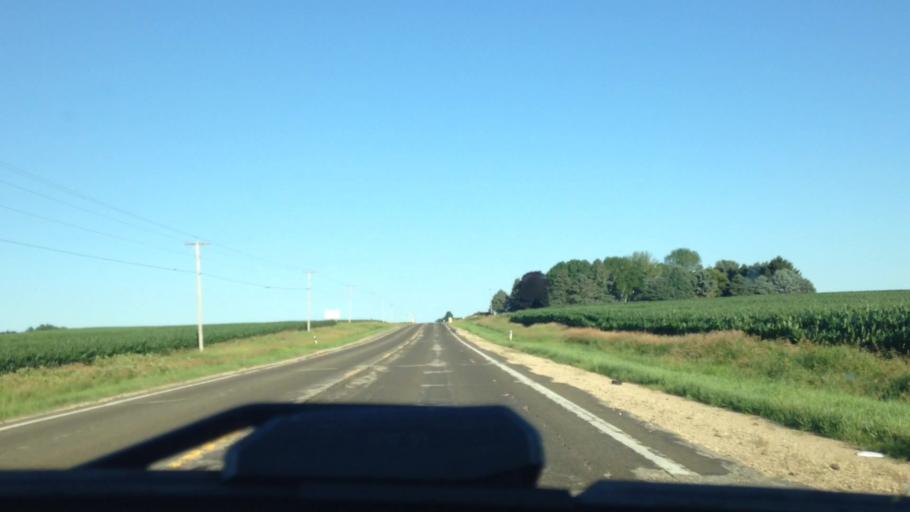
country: US
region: Wisconsin
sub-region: Columbia County
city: Poynette
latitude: 43.3375
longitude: -89.4107
